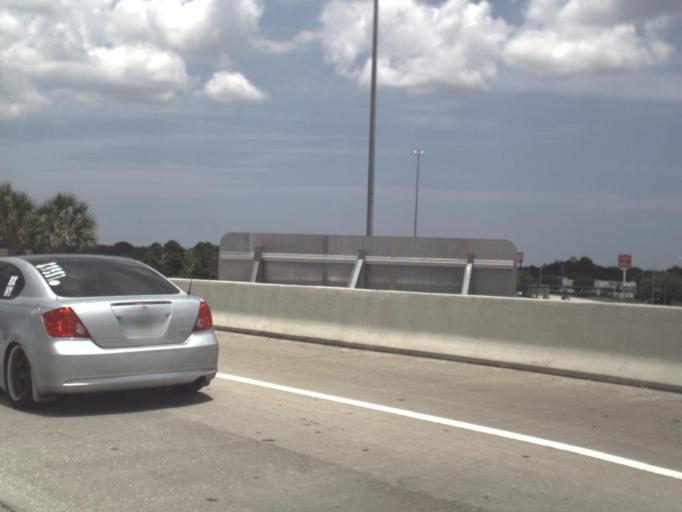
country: US
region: Florida
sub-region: Duval County
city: Jacksonville
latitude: 30.3293
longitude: -81.5540
